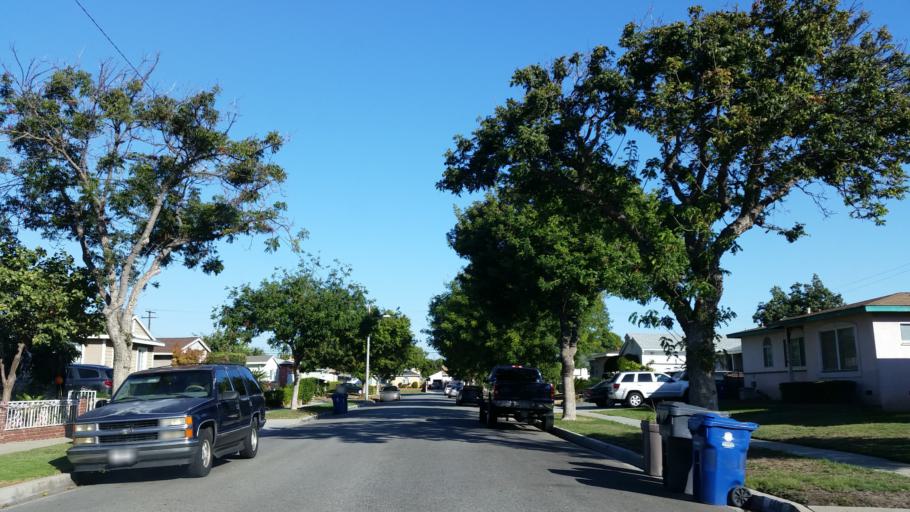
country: US
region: California
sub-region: Los Angeles County
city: Lakewood
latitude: 33.8592
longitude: -118.1136
